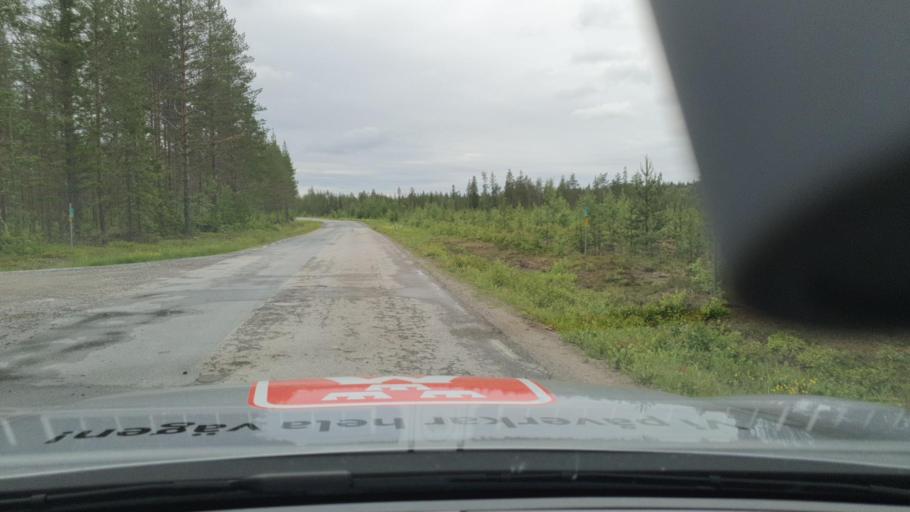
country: SE
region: Norrbotten
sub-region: Lulea Kommun
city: Ranea
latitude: 65.8013
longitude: 22.3082
